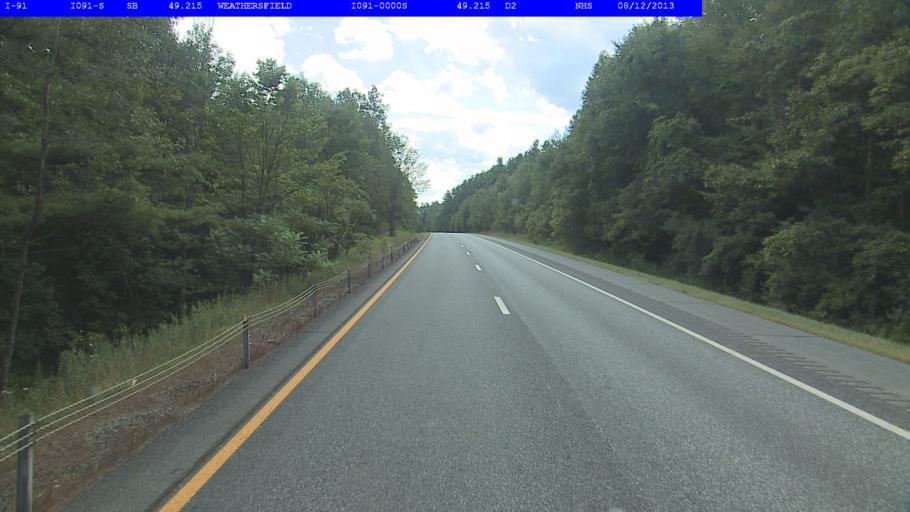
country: US
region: New Hampshire
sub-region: Sullivan County
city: Claremont
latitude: 43.3725
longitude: -72.4246
